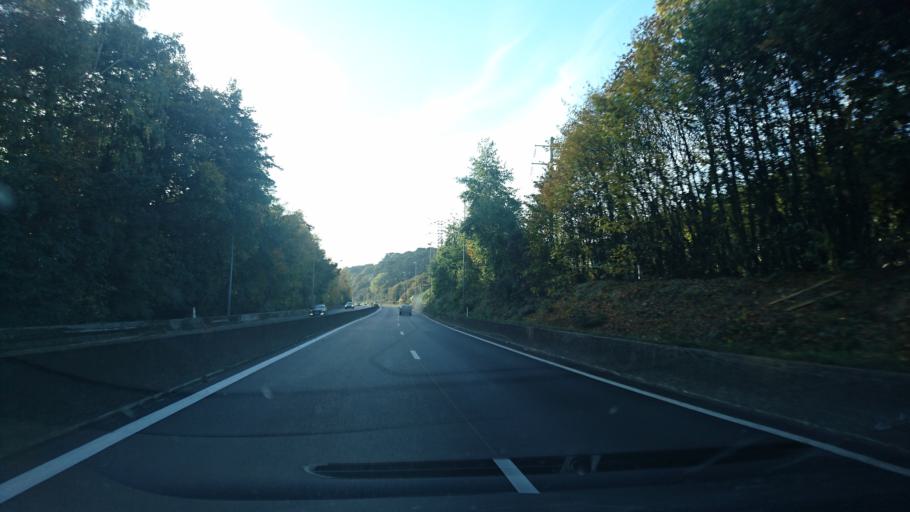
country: FR
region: Brittany
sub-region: Departement du Finistere
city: Brest
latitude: 48.3936
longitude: -4.4439
